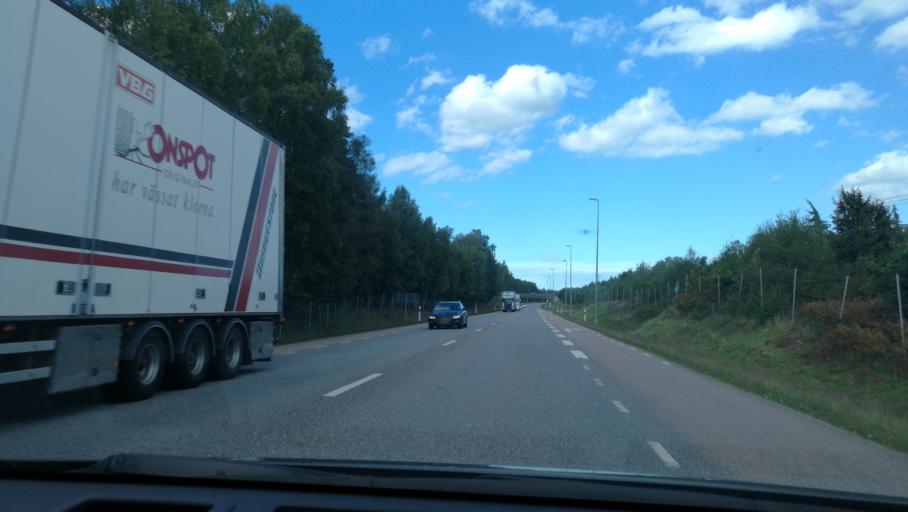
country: SE
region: Vaestra Goetaland
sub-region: Mariestads Kommun
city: Mariestad
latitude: 58.7080
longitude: 13.8750
